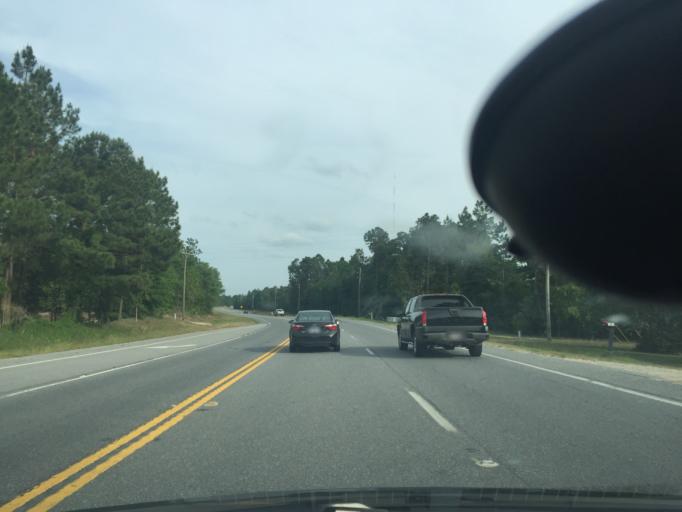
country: US
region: Georgia
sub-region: Chatham County
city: Bloomingdale
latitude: 32.0603
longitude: -81.3523
